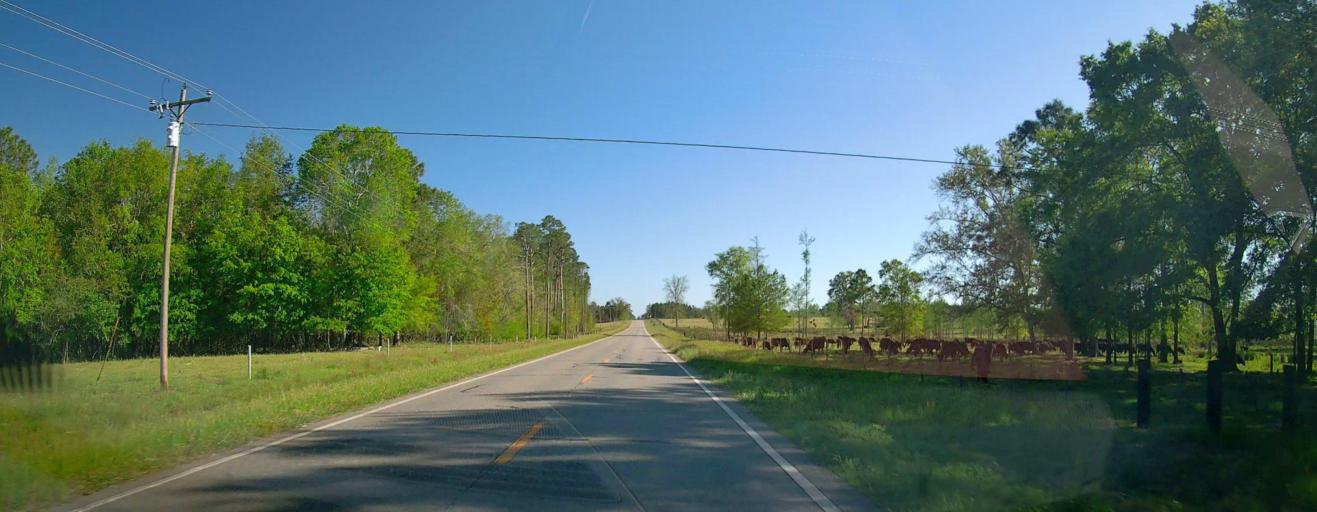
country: US
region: Georgia
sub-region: Wilcox County
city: Rochelle
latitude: 31.8523
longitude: -83.4890
